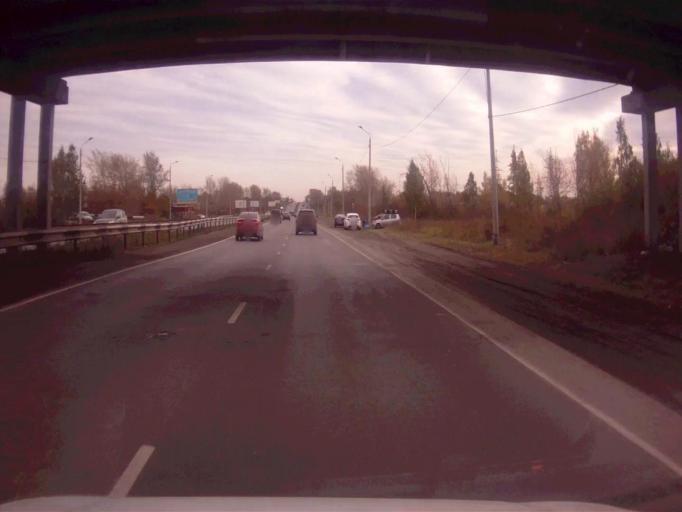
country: RU
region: Chelyabinsk
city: Novosineglazovskiy
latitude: 55.0621
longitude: 61.4000
